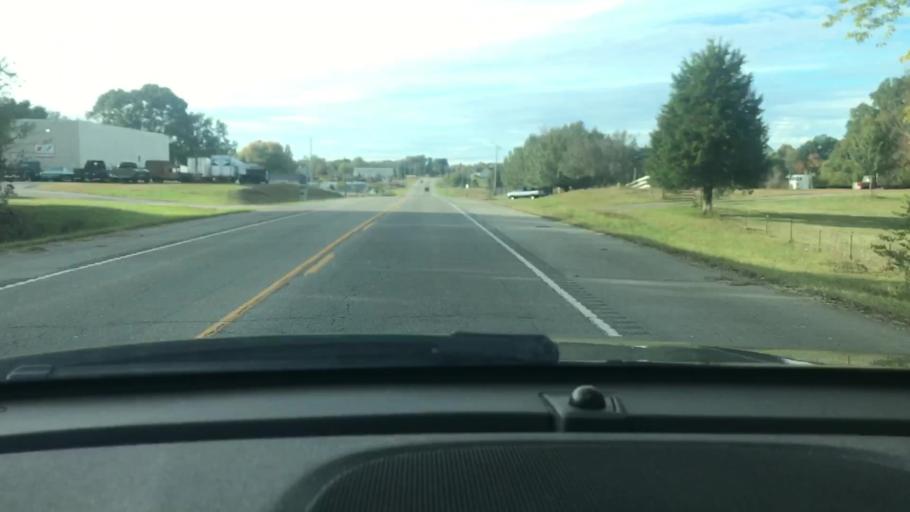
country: US
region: Tennessee
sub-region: Dickson County
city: White Bluff
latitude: 36.1295
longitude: -87.2305
